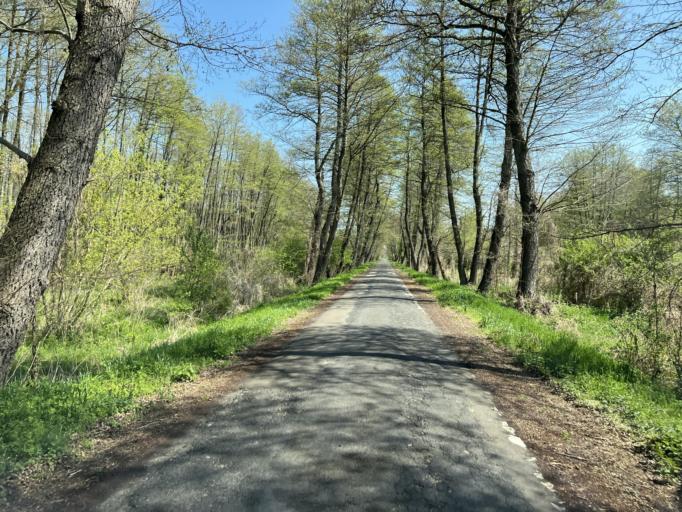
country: HU
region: Pest
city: Inarcs
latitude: 47.2601
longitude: 19.2897
